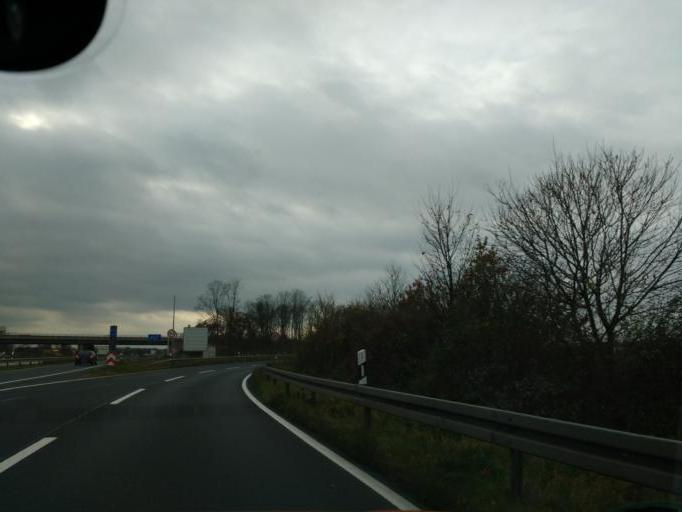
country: DE
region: Lower Saxony
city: Lehrte
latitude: 52.3607
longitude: 9.8873
